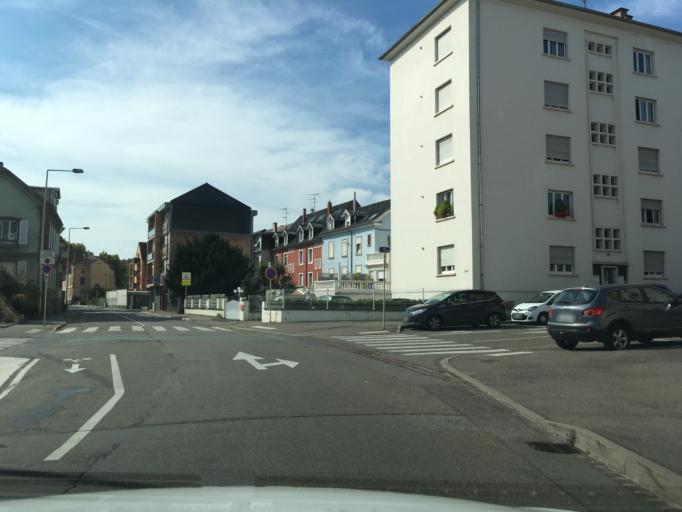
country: FR
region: Alsace
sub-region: Departement du Haut-Rhin
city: Colmar
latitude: 48.0744
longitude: 7.3621
